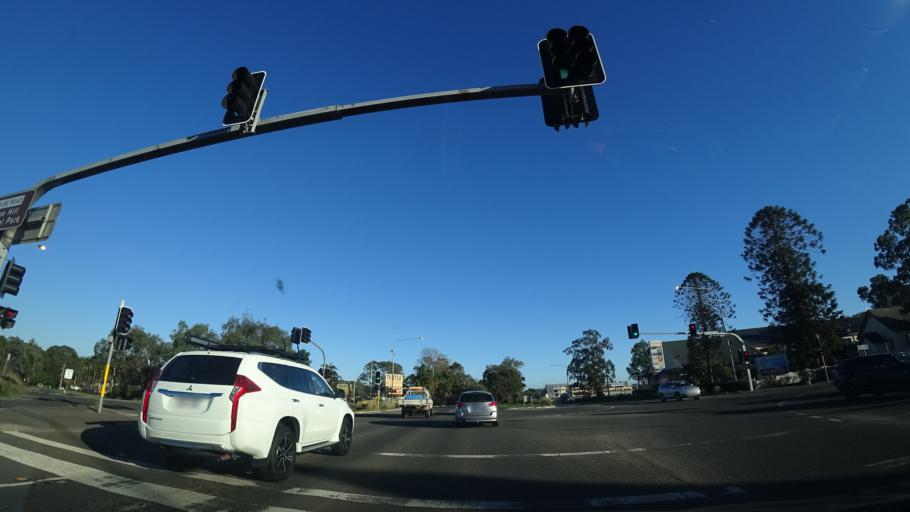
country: AU
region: New South Wales
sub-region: Blacktown
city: Rouse Hill
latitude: -33.6843
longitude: 150.9170
